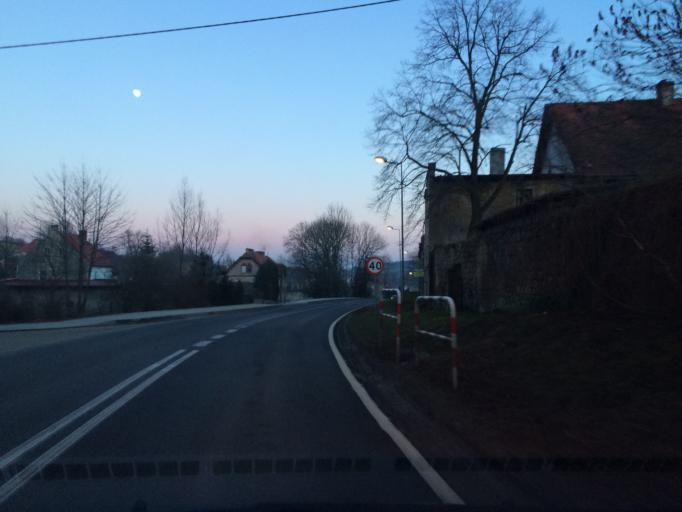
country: PL
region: Lower Silesian Voivodeship
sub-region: Powiat zlotoryjski
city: Zlotoryja
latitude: 51.1164
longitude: 15.8713
